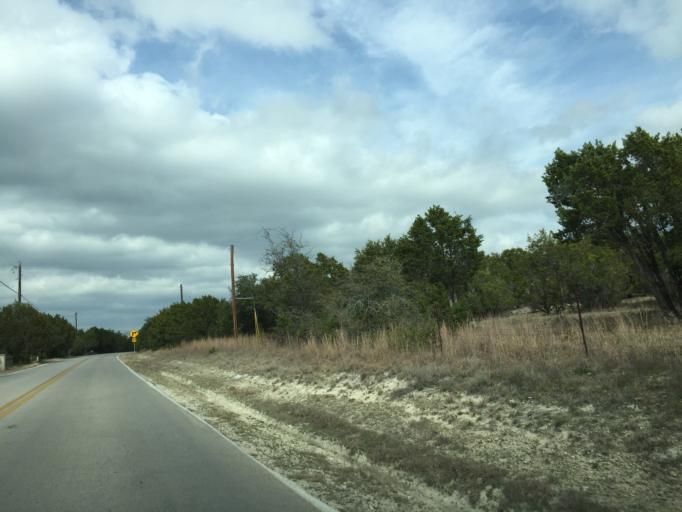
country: US
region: Texas
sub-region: Travis County
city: Briarcliff
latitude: 30.3732
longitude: -98.0860
